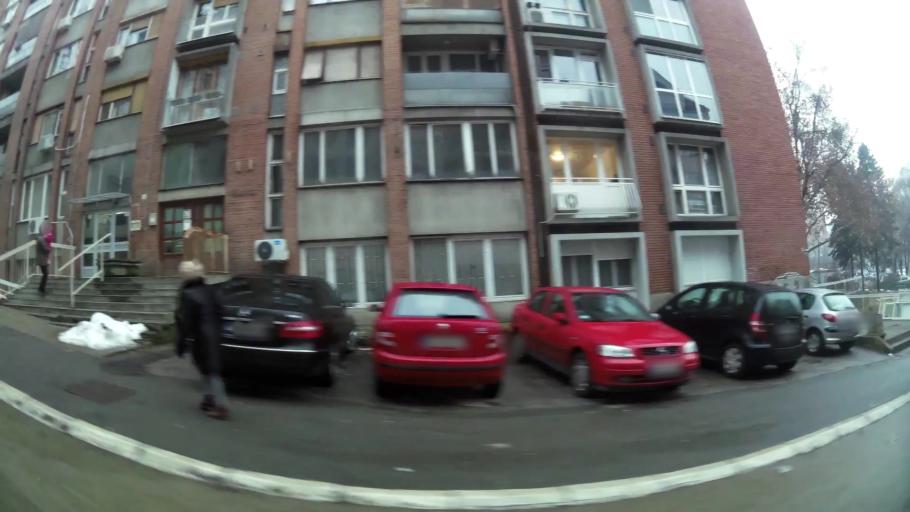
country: RS
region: Central Serbia
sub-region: Belgrade
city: Cukarica
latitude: 44.7839
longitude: 20.4216
